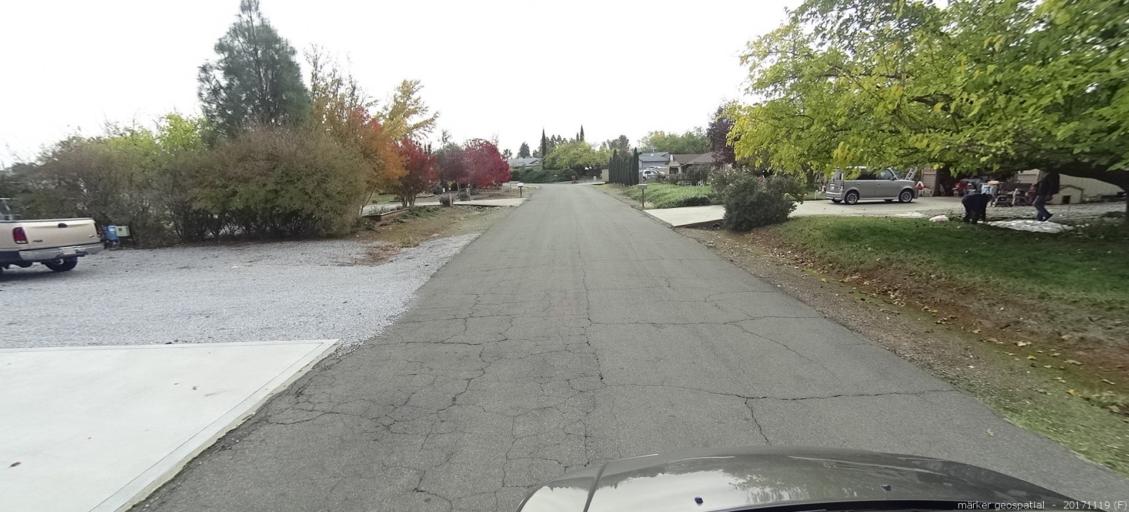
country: US
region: California
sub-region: Shasta County
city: Anderson
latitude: 40.4831
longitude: -122.2849
